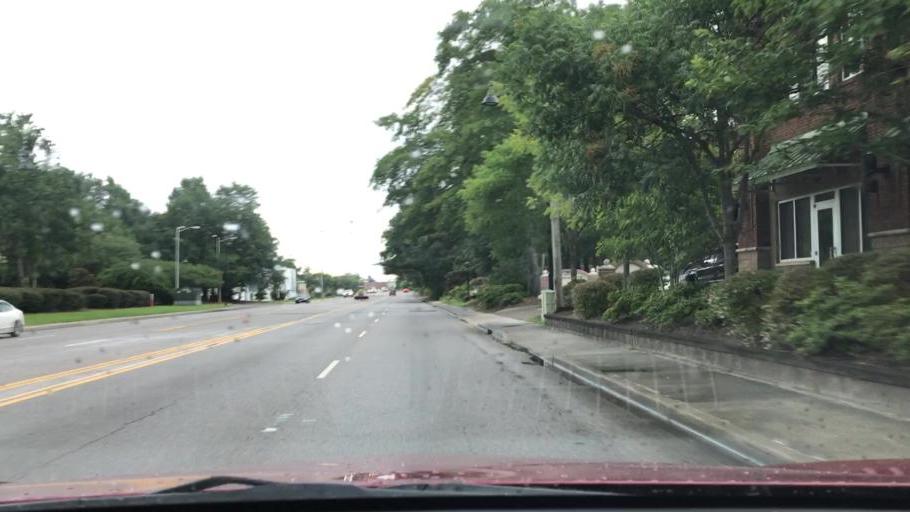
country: US
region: South Carolina
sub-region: Charleston County
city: North Charleston
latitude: 32.8635
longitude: -80.0207
